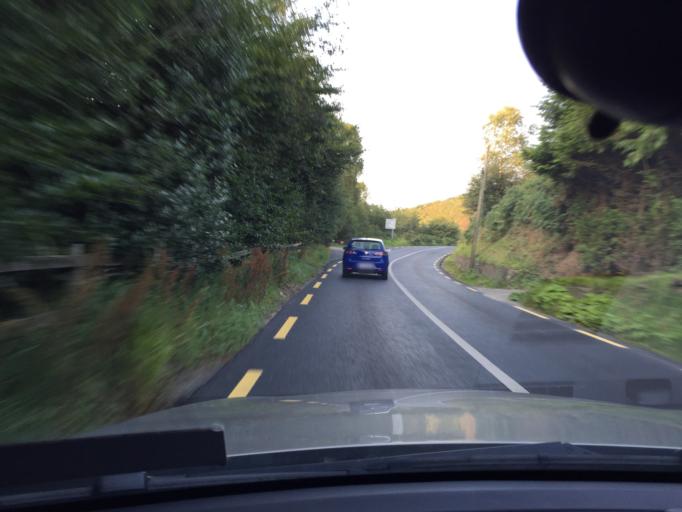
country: IE
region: Leinster
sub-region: Wicklow
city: Rathdrum
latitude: 53.0332
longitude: -6.2508
